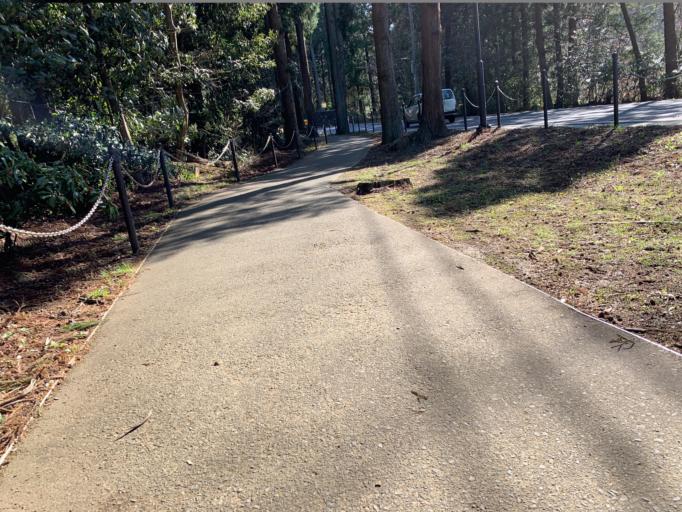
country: JP
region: Miyagi
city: Sendai
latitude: 38.2563
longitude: 140.8559
